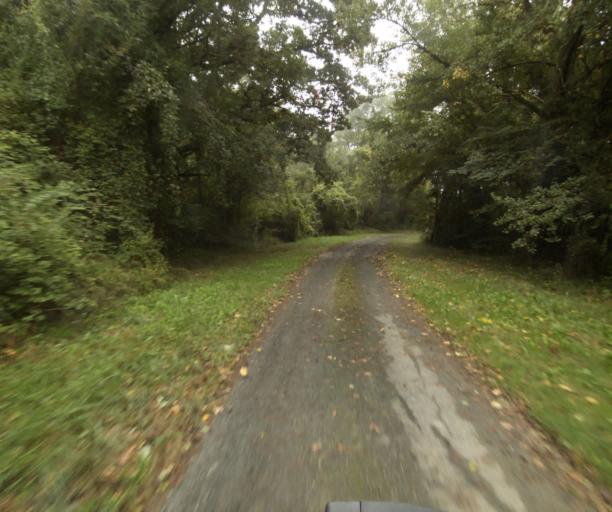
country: FR
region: Midi-Pyrenees
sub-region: Departement du Tarn-et-Garonne
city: Nohic
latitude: 43.8980
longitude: 1.4742
